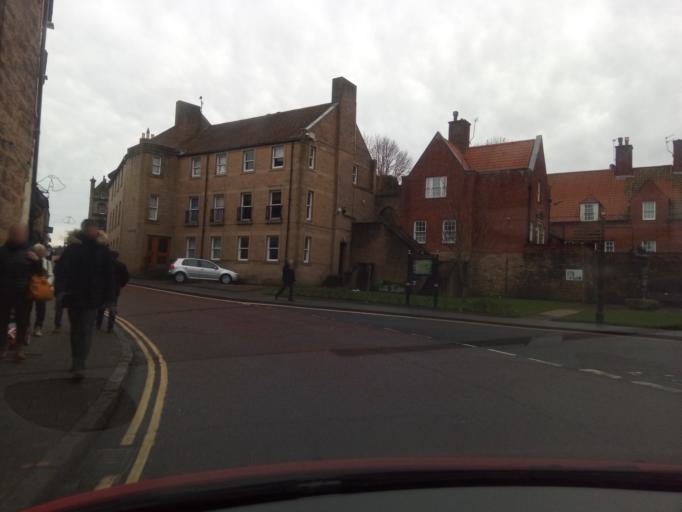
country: GB
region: England
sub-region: Northumberland
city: Alnwick
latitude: 55.4150
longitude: -1.7088
